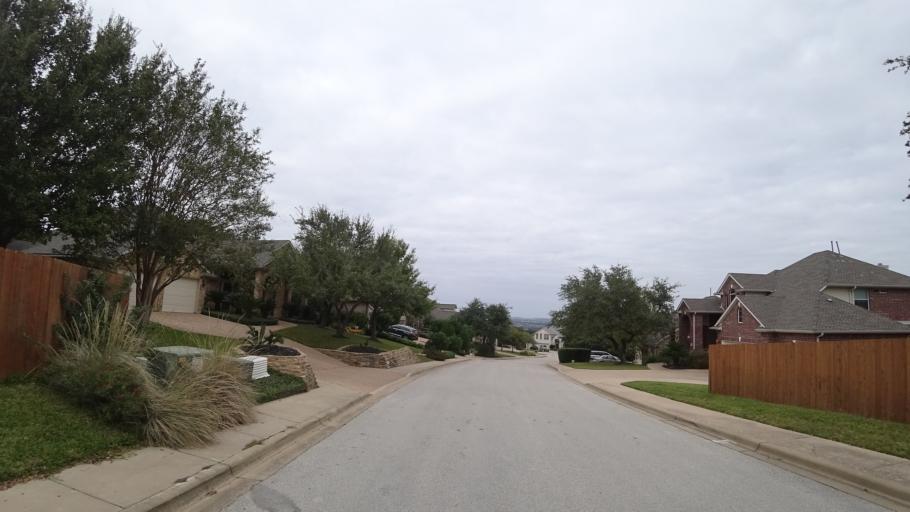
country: US
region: Texas
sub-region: Travis County
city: Bee Cave
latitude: 30.3166
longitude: -97.9166
